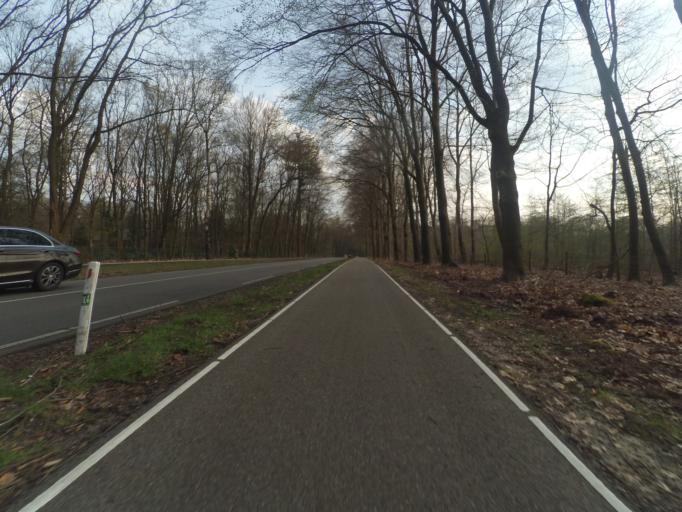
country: NL
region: Gelderland
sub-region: Gemeente Apeldoorn
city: Beekbergen
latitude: 52.1402
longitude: 5.8861
